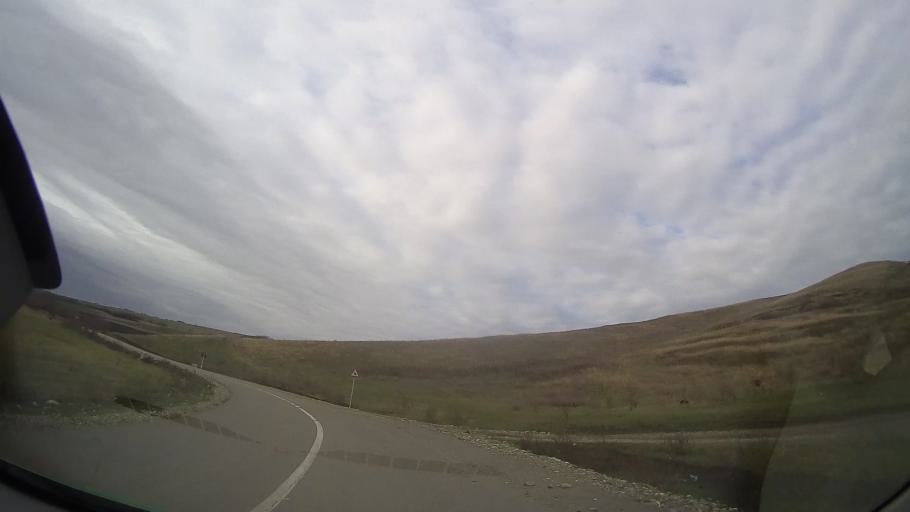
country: RO
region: Bistrita-Nasaud
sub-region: Comuna Silvasu de Campie
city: Silvasu de Campie
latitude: 46.8049
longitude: 24.3015
